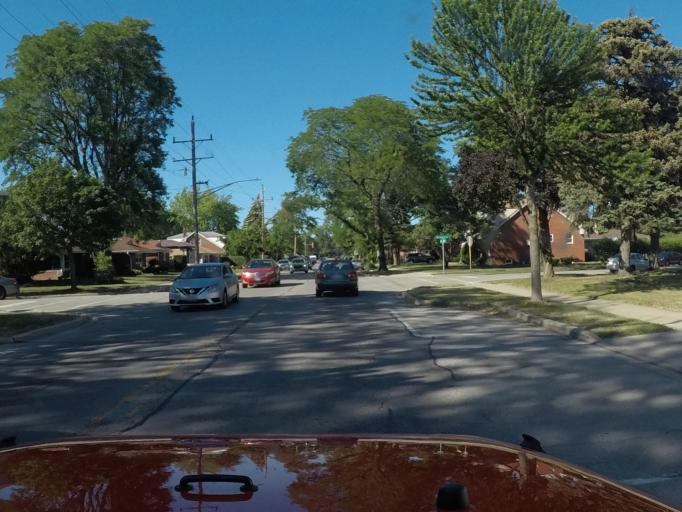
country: US
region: Illinois
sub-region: Cook County
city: Morton Grove
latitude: 42.0326
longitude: -87.7627
